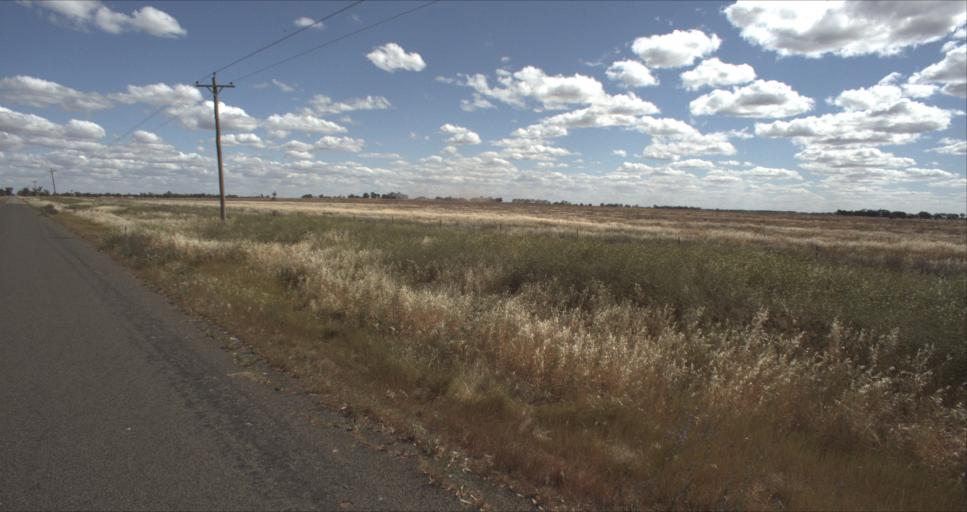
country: AU
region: New South Wales
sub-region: Leeton
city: Leeton
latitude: -34.4722
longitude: 146.2507
